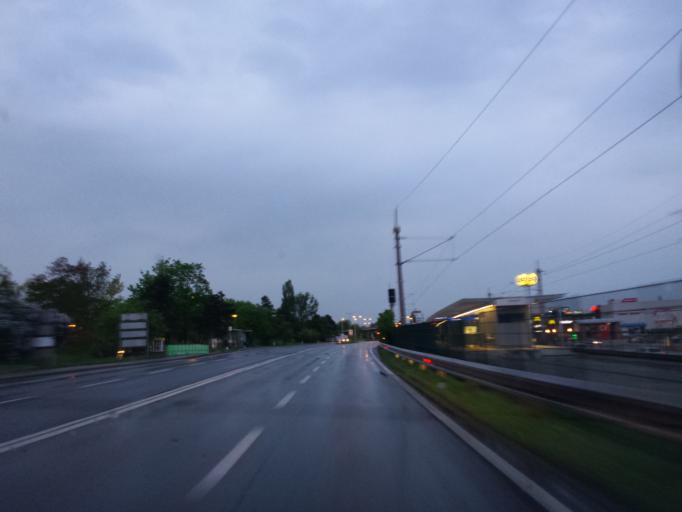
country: AT
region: Lower Austria
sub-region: Politischer Bezirk Modling
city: Vosendorf
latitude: 48.1109
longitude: 16.3153
